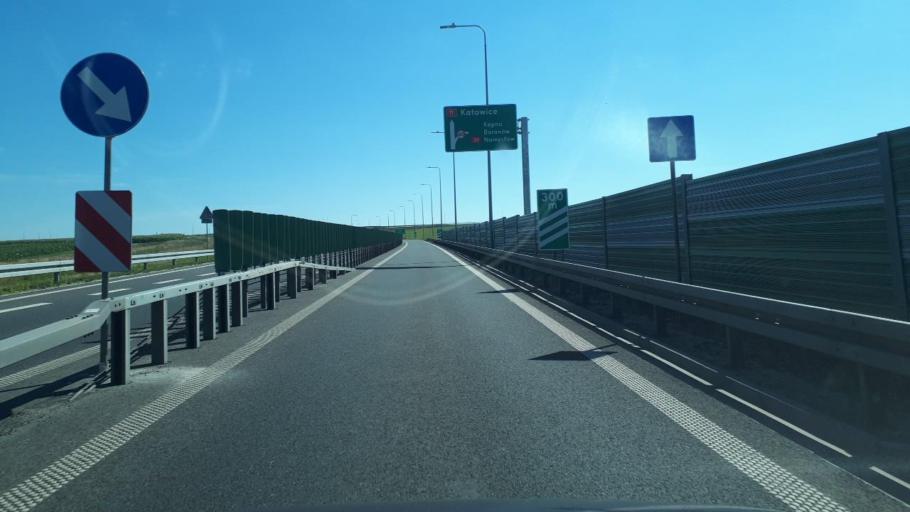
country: PL
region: Greater Poland Voivodeship
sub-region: Powiat kepinski
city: Baranow
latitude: 51.2602
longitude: 18.0177
